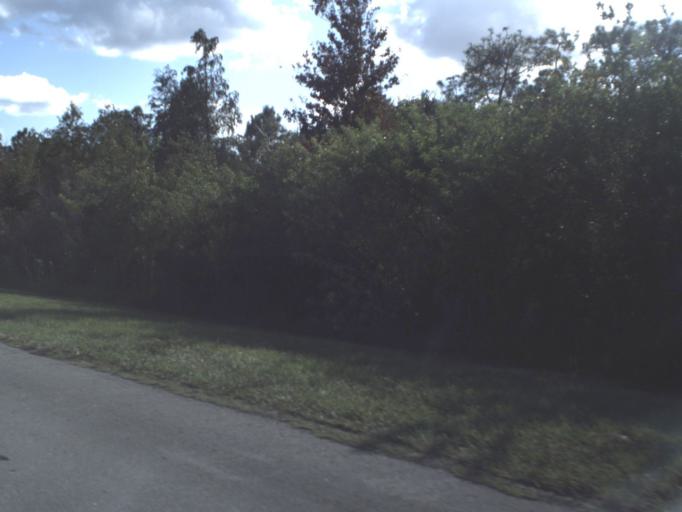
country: US
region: Florida
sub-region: Orange County
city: Southchase
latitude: 28.3986
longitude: -81.3915
